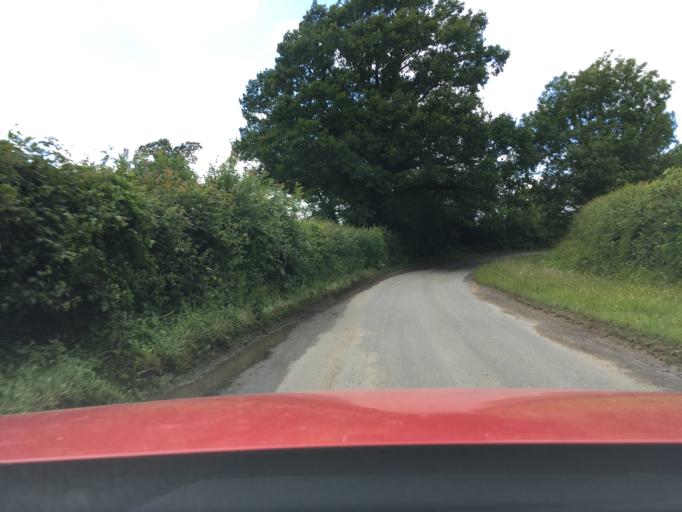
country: GB
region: England
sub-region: Gloucestershire
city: Gloucester
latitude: 51.8321
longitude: -2.3269
